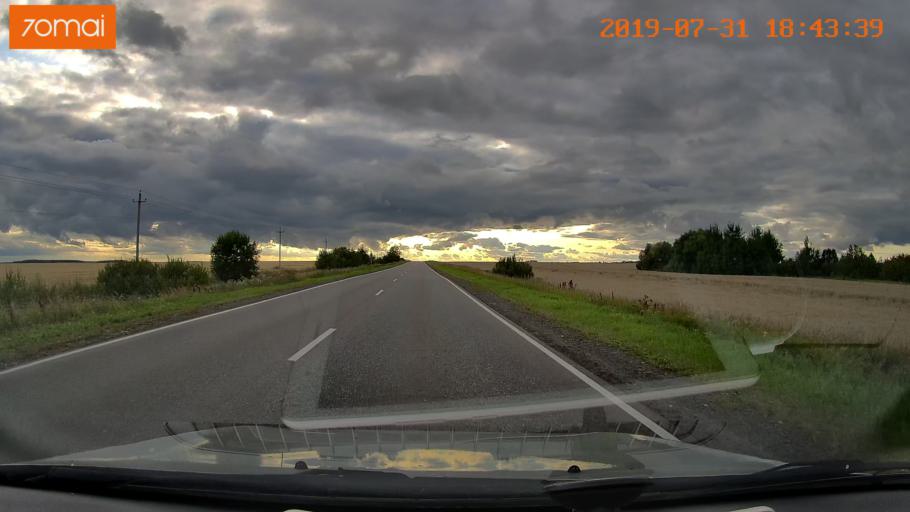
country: RU
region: Moskovskaya
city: Troitskoye
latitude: 55.2457
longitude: 38.5712
